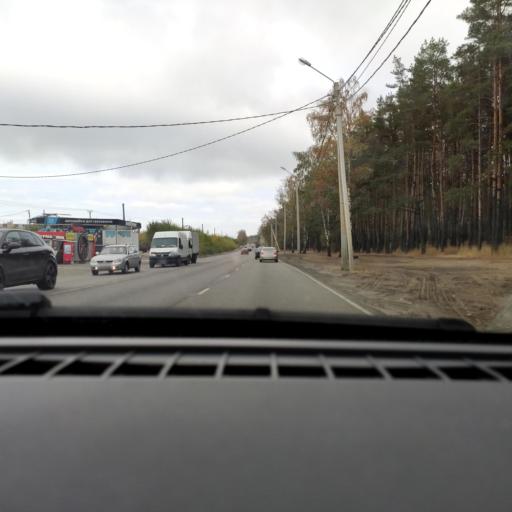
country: RU
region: Voronezj
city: Voronezh
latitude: 51.6727
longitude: 39.2723
